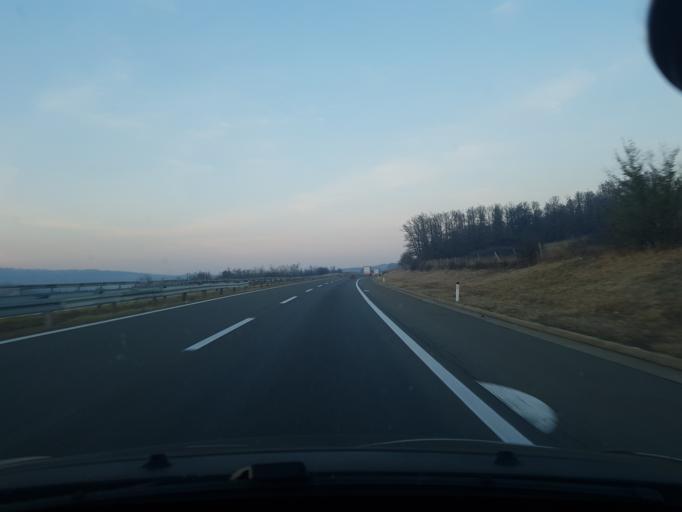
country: RS
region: Central Serbia
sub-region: Nisavski Okrug
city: Razanj
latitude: 43.6464
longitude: 21.5551
